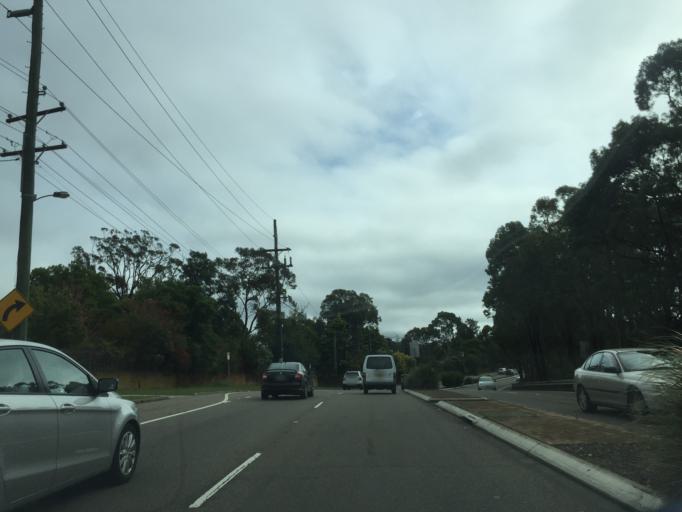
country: AU
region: New South Wales
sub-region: Blue Mountains Municipality
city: Blaxland
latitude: -33.7335
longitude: 150.6045
